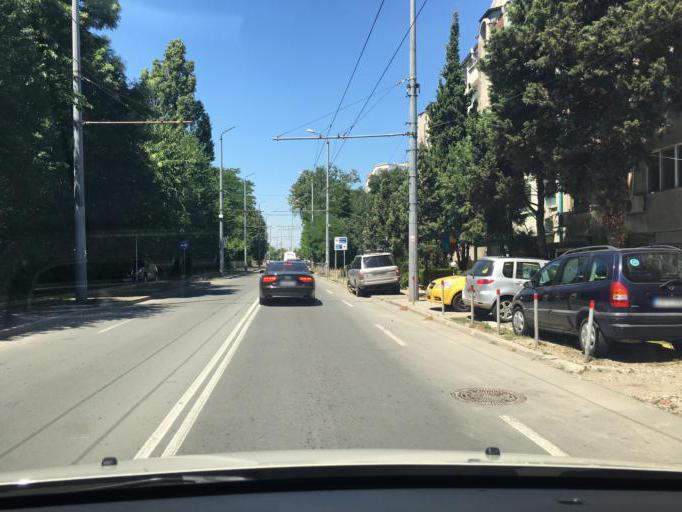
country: BG
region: Burgas
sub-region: Obshtina Burgas
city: Burgas
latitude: 42.4909
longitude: 27.4635
